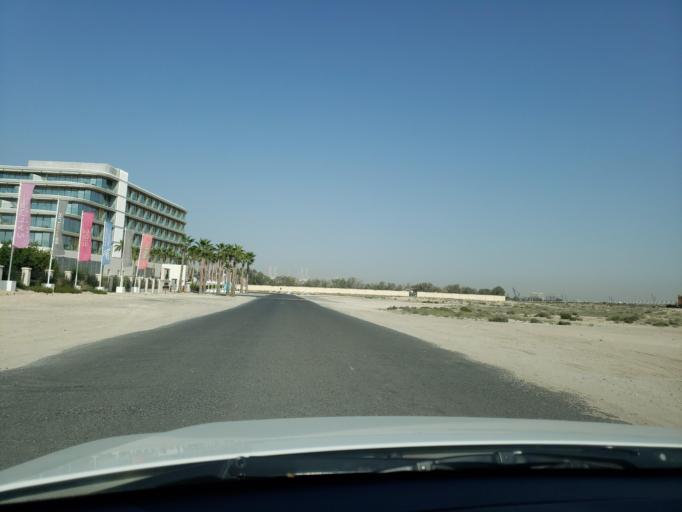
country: AE
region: Dubai
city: Dubai
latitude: 24.9798
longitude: 55.0247
